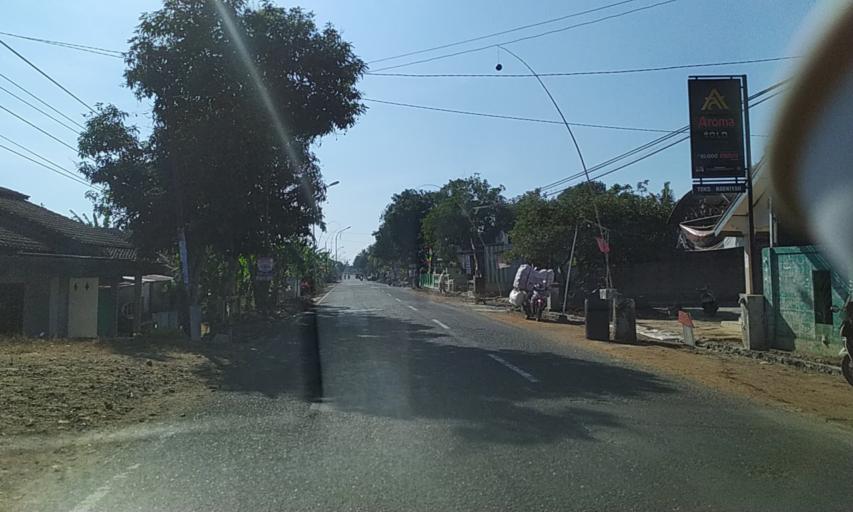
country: ID
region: Central Java
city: Kroya
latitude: -7.6337
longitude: 109.2578
